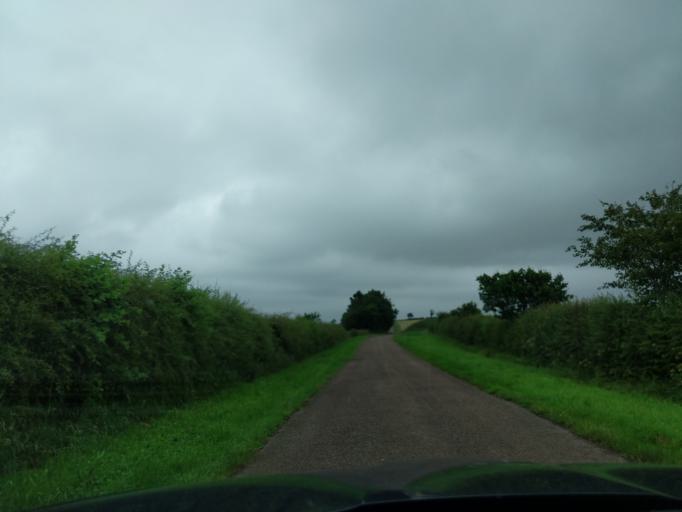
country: GB
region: England
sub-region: Northumberland
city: Ford
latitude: 55.6873
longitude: -2.1269
